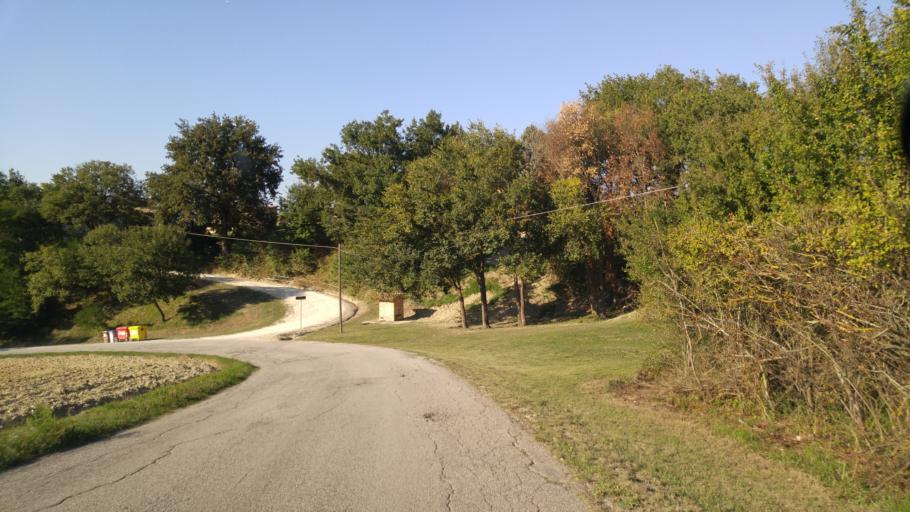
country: IT
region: The Marches
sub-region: Provincia di Pesaro e Urbino
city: Fermignano
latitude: 43.6634
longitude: 12.6493
